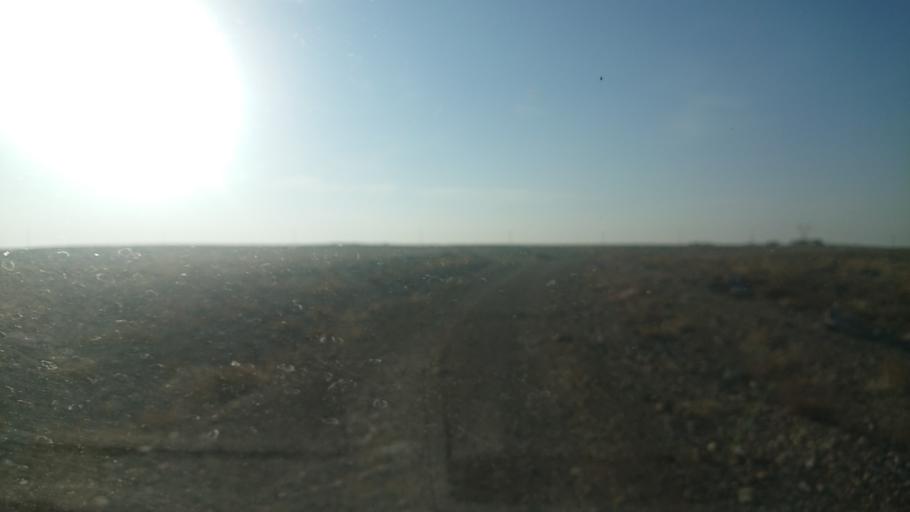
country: TR
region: Aksaray
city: Sultanhani
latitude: 38.1454
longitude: 33.5828
